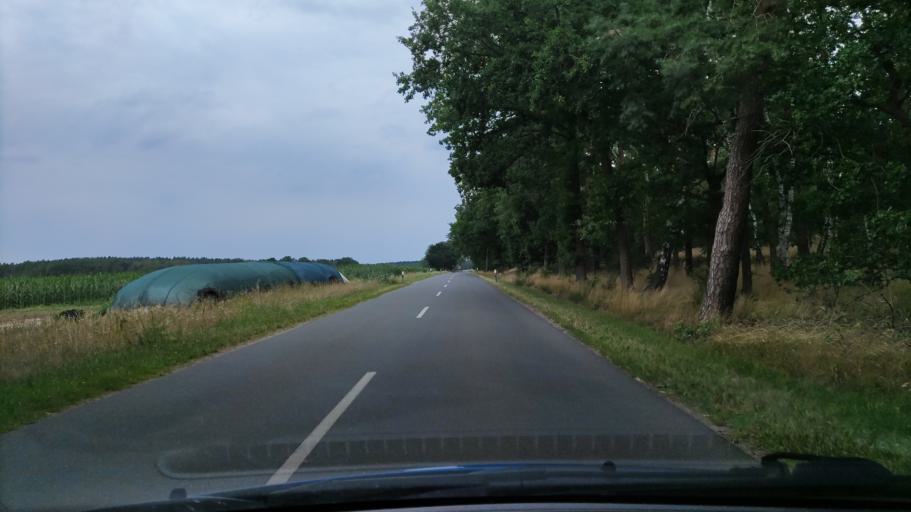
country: DE
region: Lower Saxony
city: Suhlendorf
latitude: 52.9547
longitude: 10.8261
